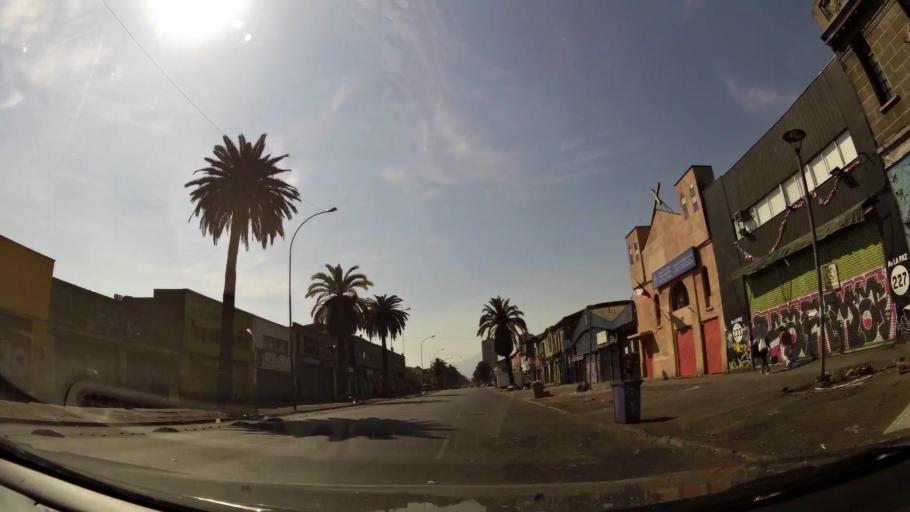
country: CL
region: Santiago Metropolitan
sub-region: Provincia de Santiago
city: Santiago
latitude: -33.4300
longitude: -70.6515
